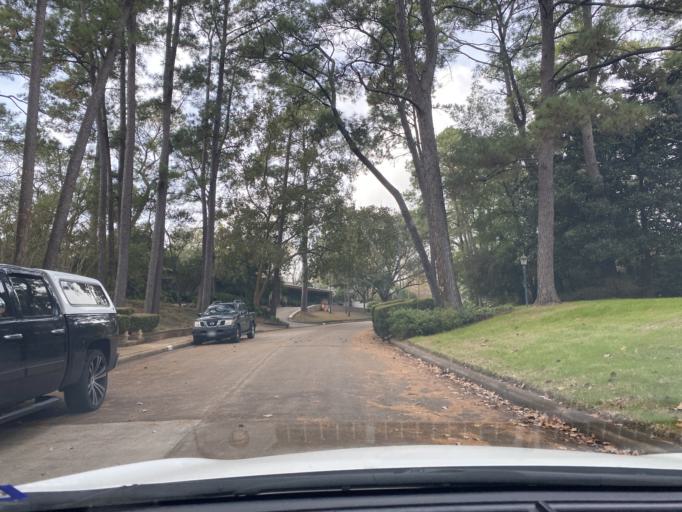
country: US
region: Texas
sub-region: Harris County
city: Hunters Creek Village
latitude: 29.7673
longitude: -95.4662
